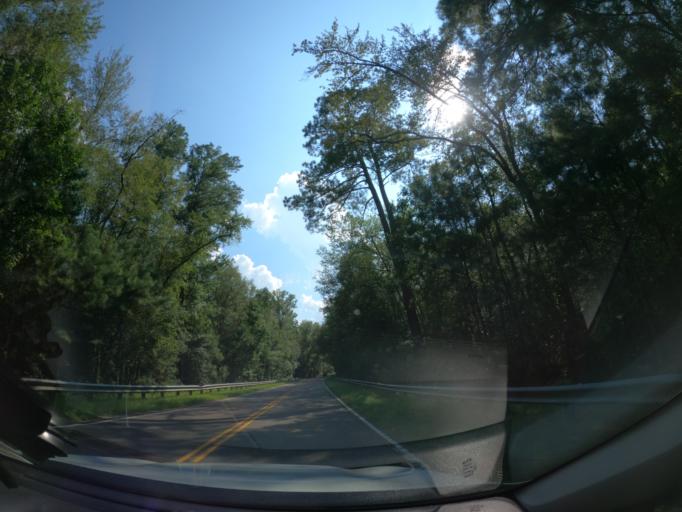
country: US
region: South Carolina
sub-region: Barnwell County
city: Williston
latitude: 33.5551
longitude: -81.4841
